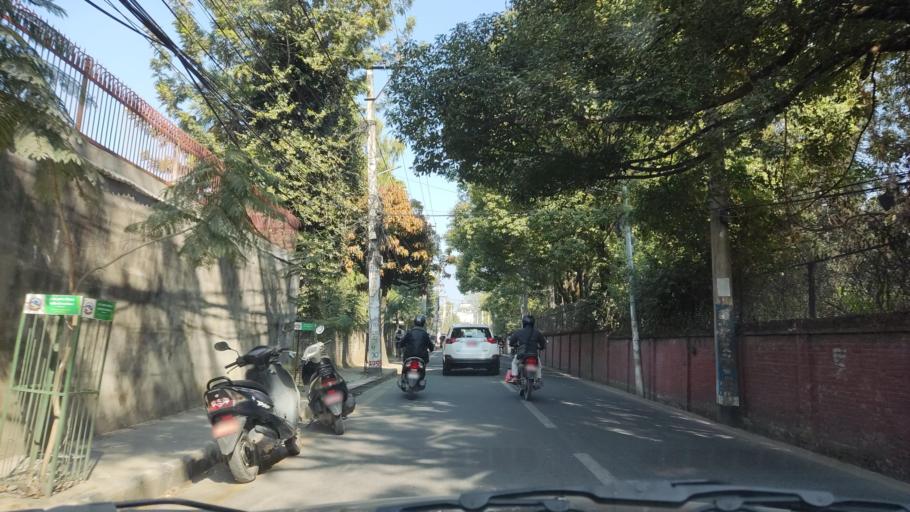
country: NP
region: Central Region
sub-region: Bagmati Zone
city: Kathmandu
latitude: 27.7195
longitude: 85.3341
